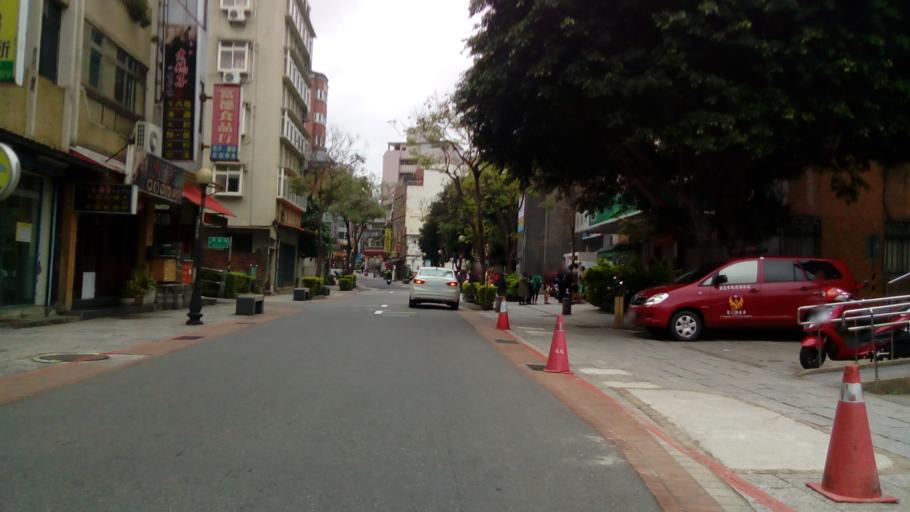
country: TW
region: Taipei
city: Taipei
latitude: 25.1722
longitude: 121.4373
